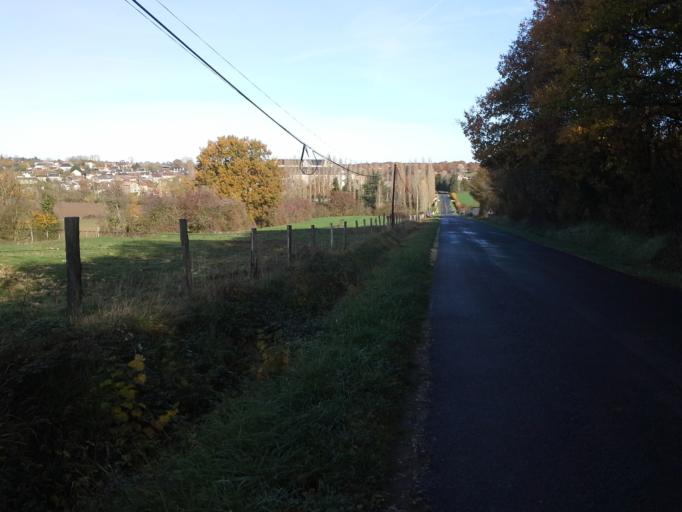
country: FR
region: Poitou-Charentes
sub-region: Departement de la Vienne
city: Pleumartin
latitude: 46.6364
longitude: 0.7535
